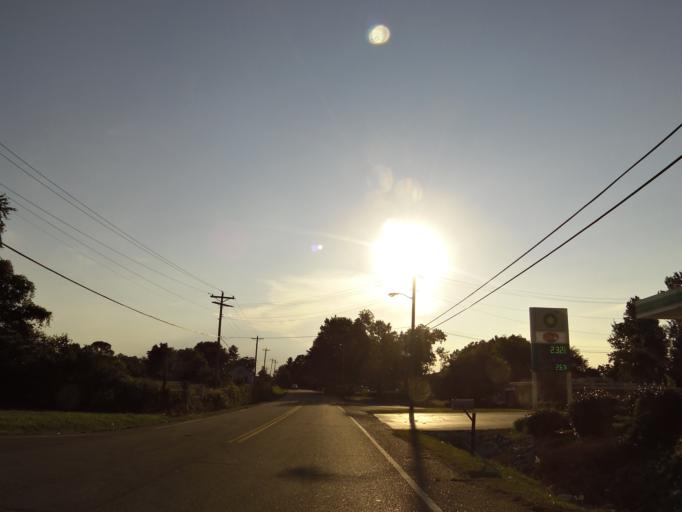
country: US
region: Tennessee
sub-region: McMinn County
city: Englewood
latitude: 35.4270
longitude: -84.4941
